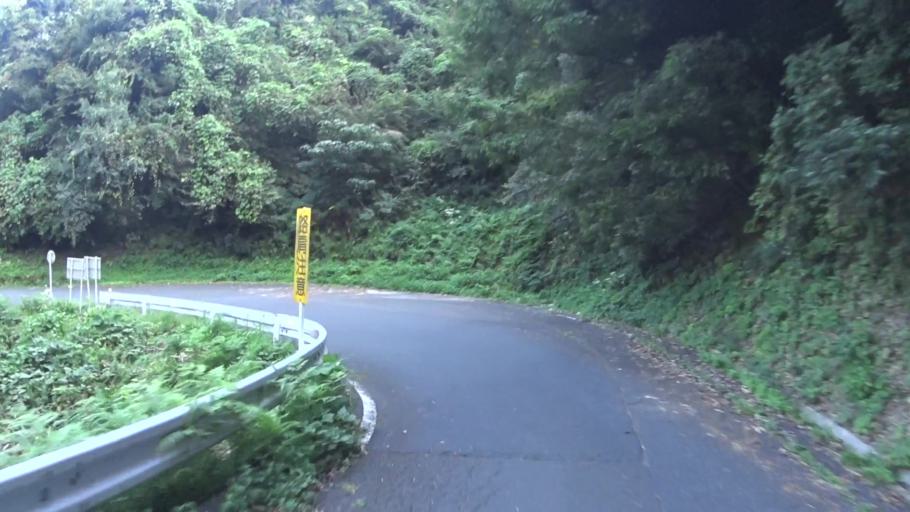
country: JP
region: Kyoto
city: Miyazu
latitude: 35.5682
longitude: 135.1389
